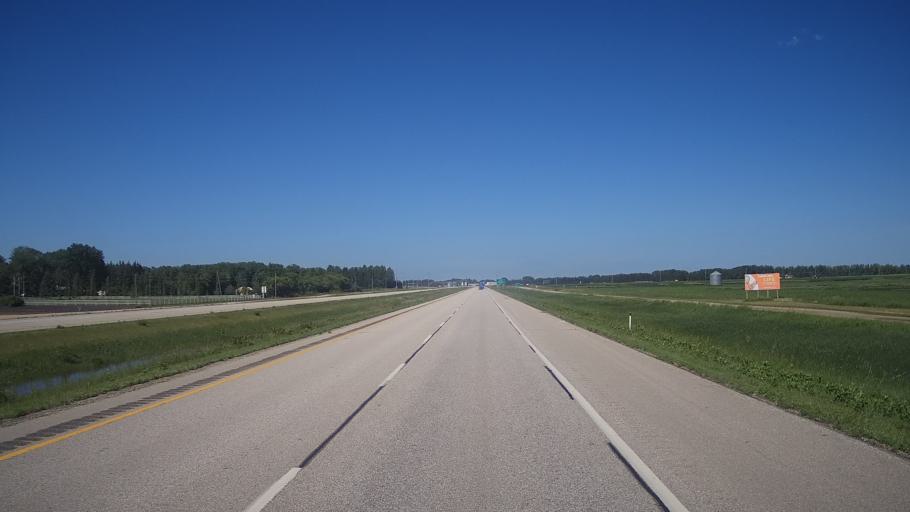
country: CA
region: Manitoba
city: Portage la Prairie
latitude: 49.9602
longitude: -98.2471
